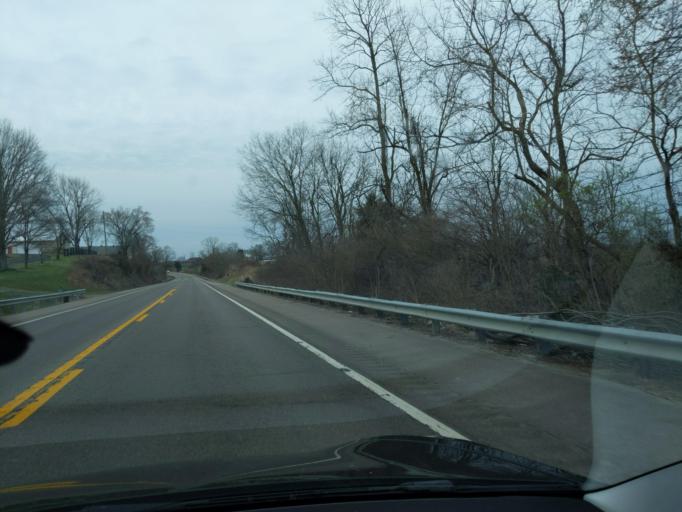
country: US
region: Kentucky
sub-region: Madison County
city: Richmond
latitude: 37.8789
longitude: -84.2977
